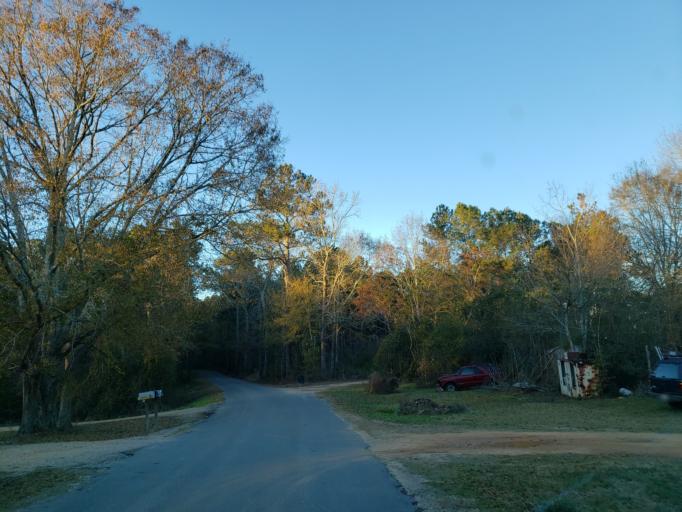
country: US
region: Mississippi
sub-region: Covington County
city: Collins
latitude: 31.5690
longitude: -89.4390
